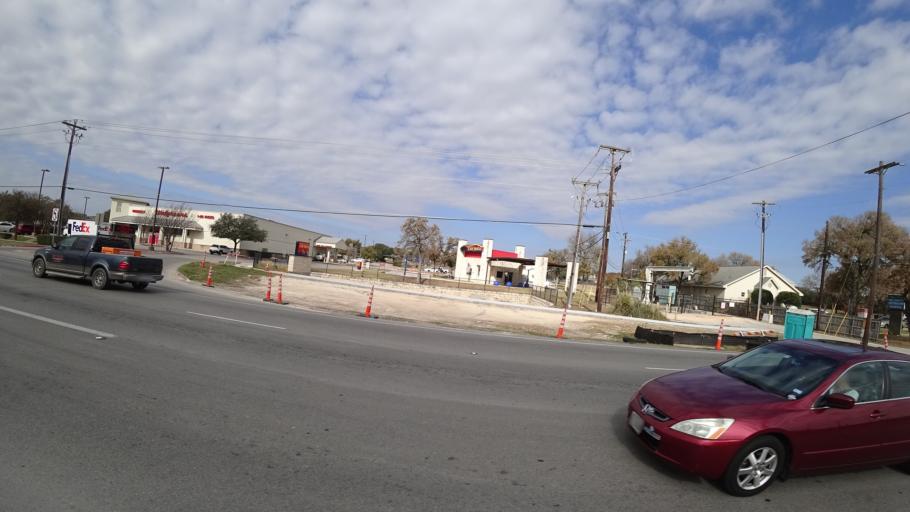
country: US
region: Texas
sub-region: Williamson County
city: Cedar Park
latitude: 30.5147
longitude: -97.8500
